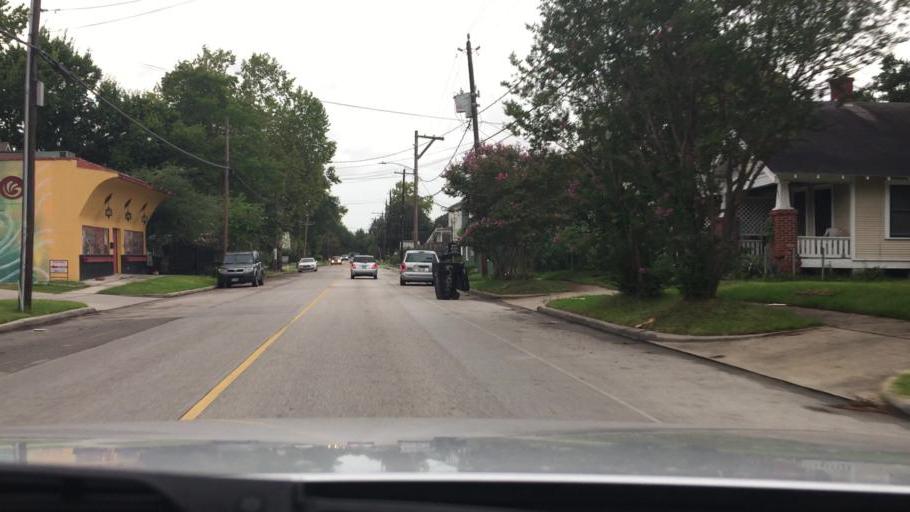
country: US
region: Texas
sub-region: Harris County
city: Houston
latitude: 29.7906
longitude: -95.3763
